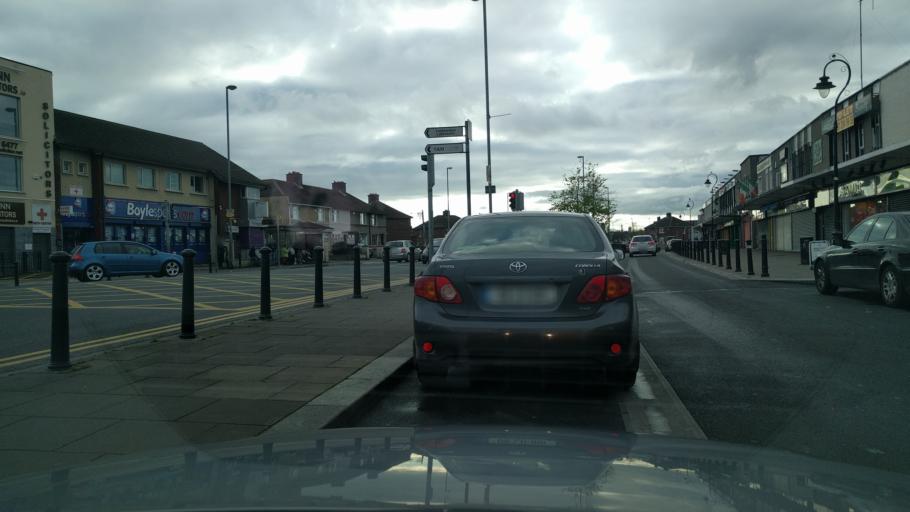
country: IE
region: Leinster
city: Ballyfermot
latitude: 53.3423
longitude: -6.3522
